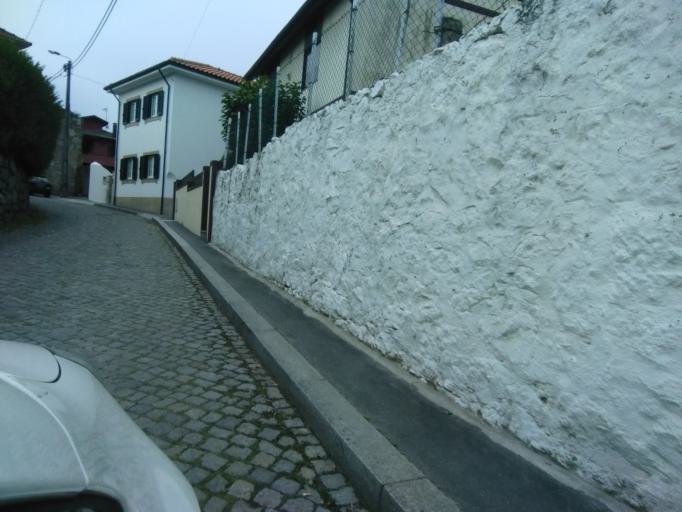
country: PT
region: Porto
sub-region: Matosinhos
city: Lavra
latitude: 41.2343
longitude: -8.7158
